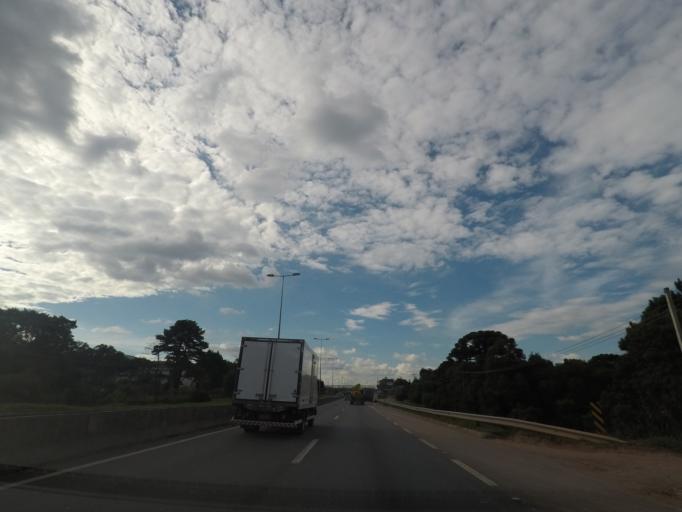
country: BR
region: Parana
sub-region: Araucaria
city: Araucaria
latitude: -25.5707
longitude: -49.3108
